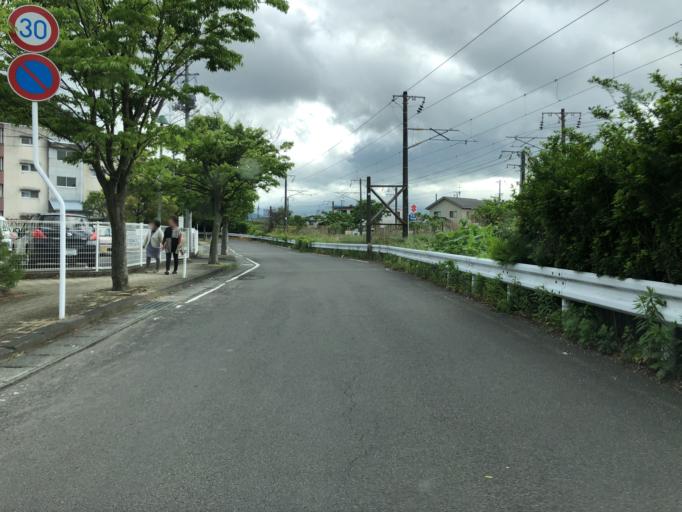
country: JP
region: Fukushima
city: Fukushima-shi
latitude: 37.7740
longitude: 140.4548
